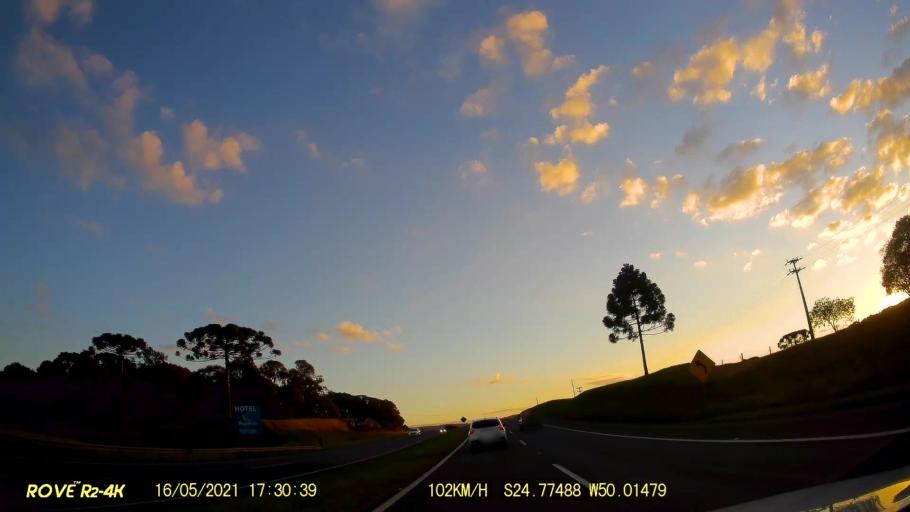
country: BR
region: Parana
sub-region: Castro
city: Castro
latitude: -24.7754
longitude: -50.0158
